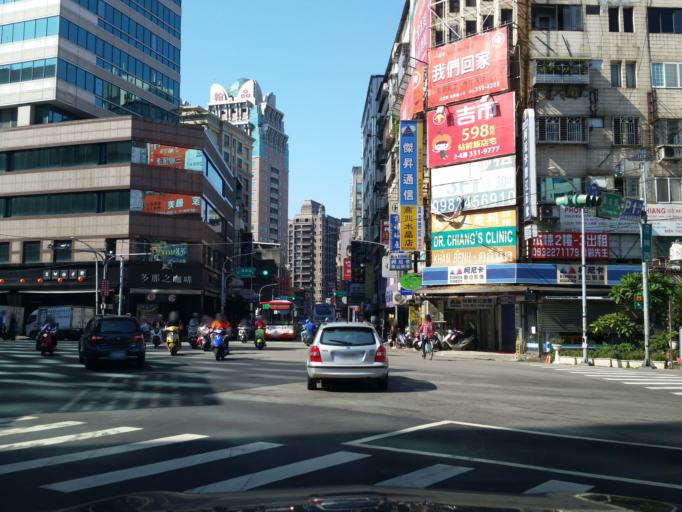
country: TW
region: Taiwan
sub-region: Taoyuan
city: Taoyuan
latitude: 24.9908
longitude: 121.3152
